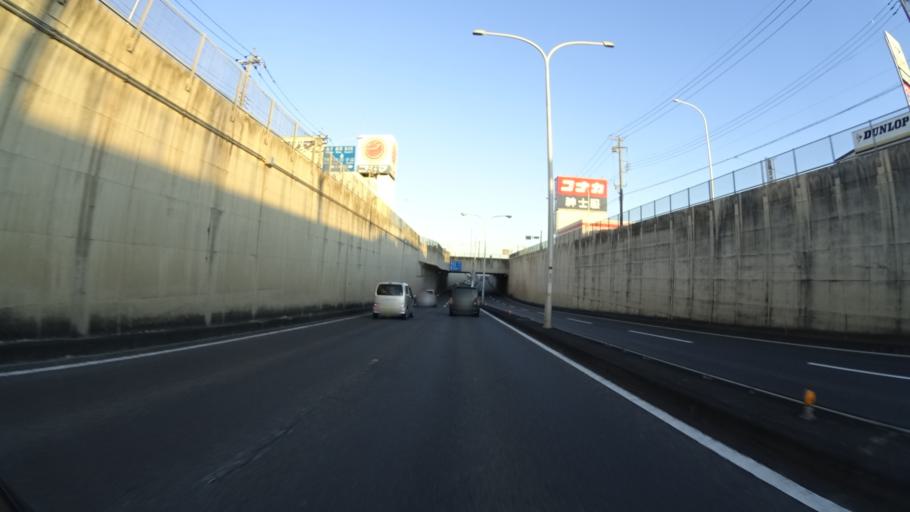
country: JP
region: Tochigi
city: Utsunomiya-shi
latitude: 36.5052
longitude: 139.8737
